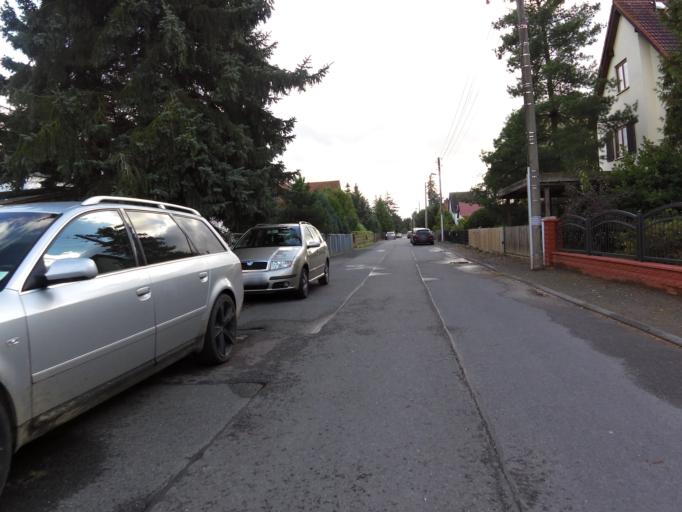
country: DE
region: Saxony
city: Taucha
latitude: 51.3273
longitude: 12.4763
